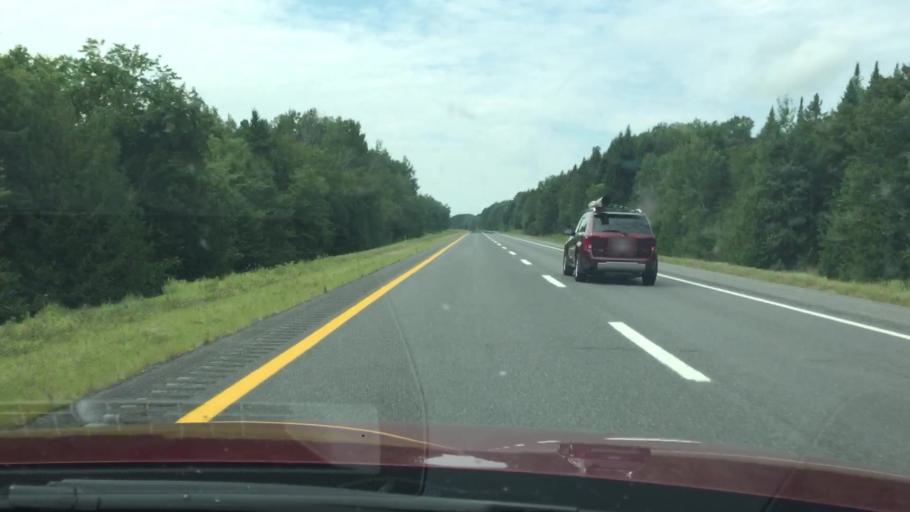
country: US
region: Maine
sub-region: Aroostook County
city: Houlton
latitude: 46.1395
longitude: -67.9228
